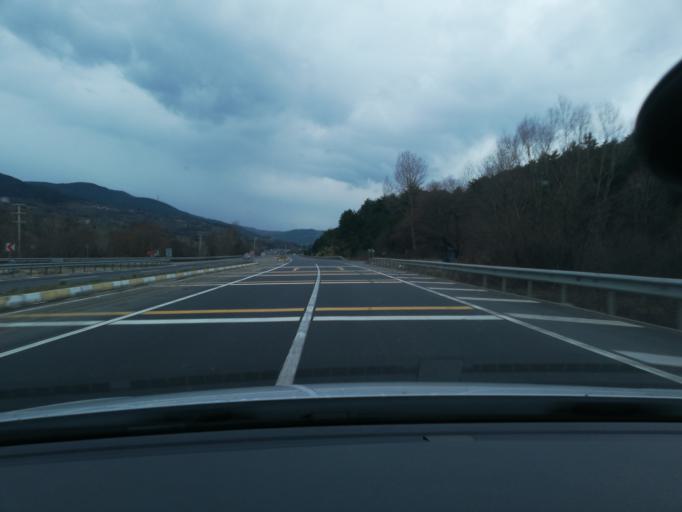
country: TR
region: Bolu
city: Yenicaga
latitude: 40.7444
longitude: 31.8533
